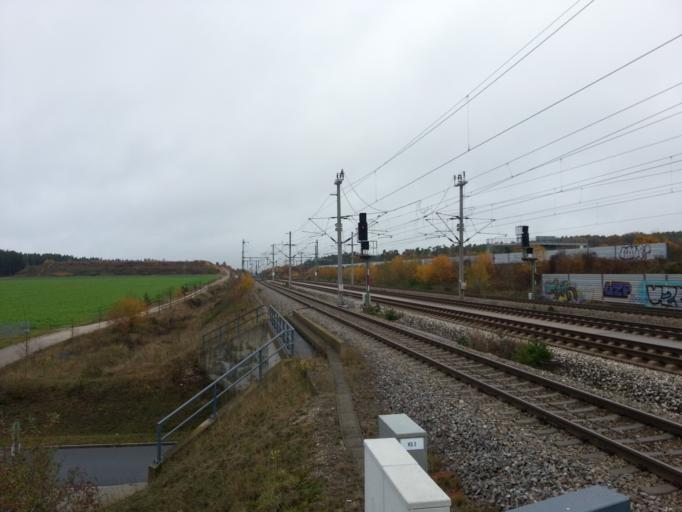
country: DE
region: Bavaria
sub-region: Regierungsbezirk Mittelfranken
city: Allersberg
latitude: 49.2624
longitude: 11.2123
